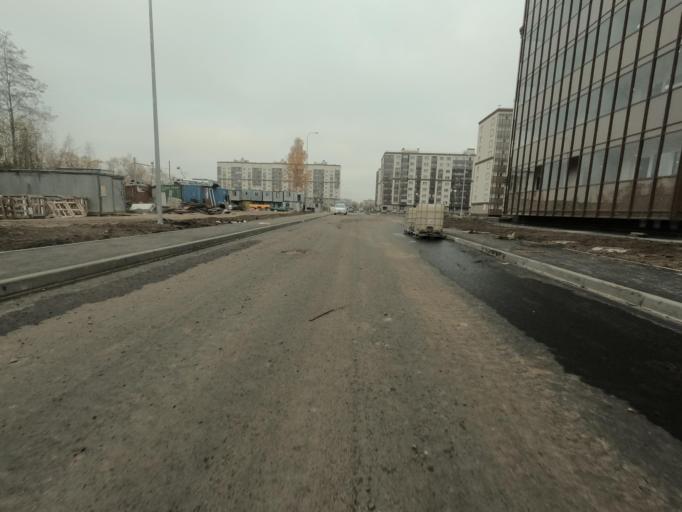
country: RU
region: Leningrad
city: Kirovsk
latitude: 59.8784
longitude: 31.0095
